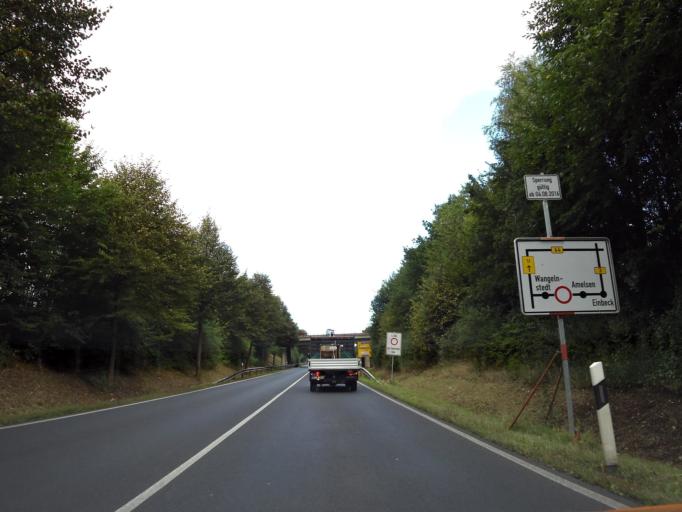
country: DE
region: Lower Saxony
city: Einbeck
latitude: 51.8193
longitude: 9.8342
